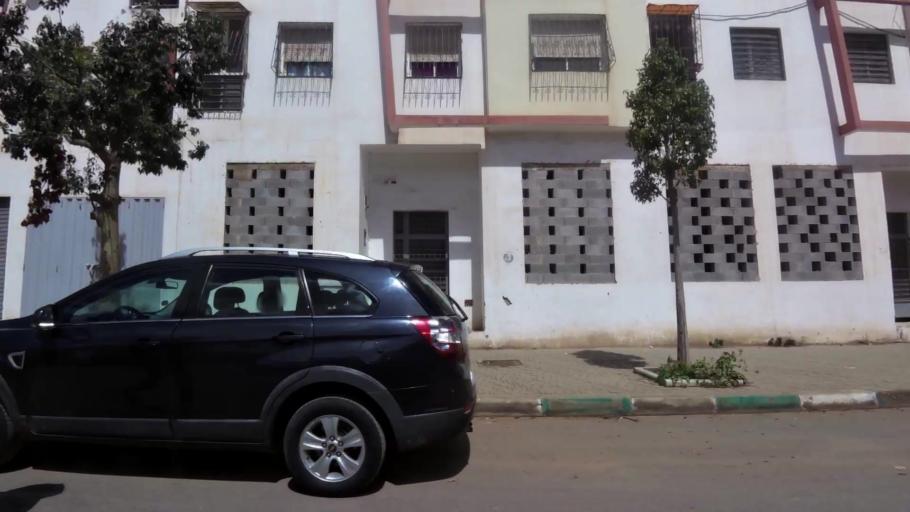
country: MA
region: Grand Casablanca
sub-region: Nouaceur
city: Dar Bouazza
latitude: 33.5354
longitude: -7.7341
